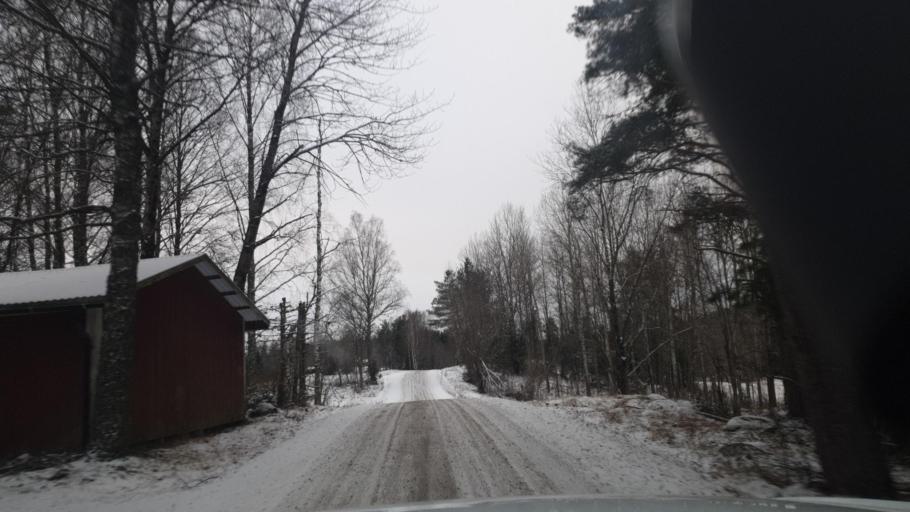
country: SE
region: Vaermland
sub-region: Karlstads Kommun
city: Edsvalla
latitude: 59.6178
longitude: 13.0671
